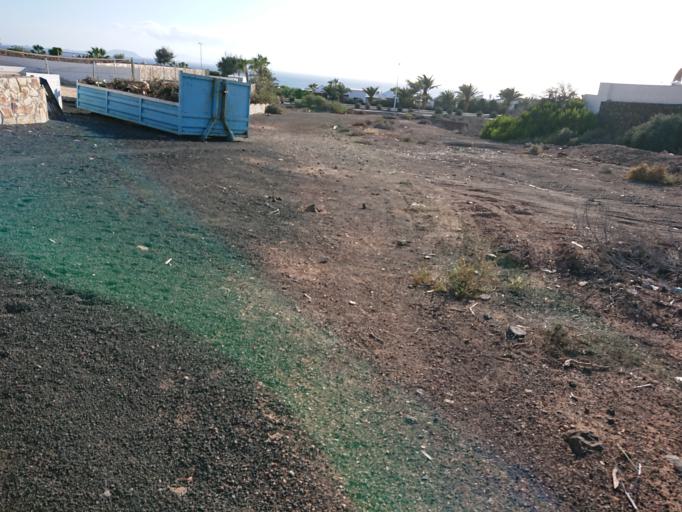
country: ES
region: Canary Islands
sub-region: Provincia de Las Palmas
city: Playa Blanca
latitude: 28.8665
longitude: -13.8480
